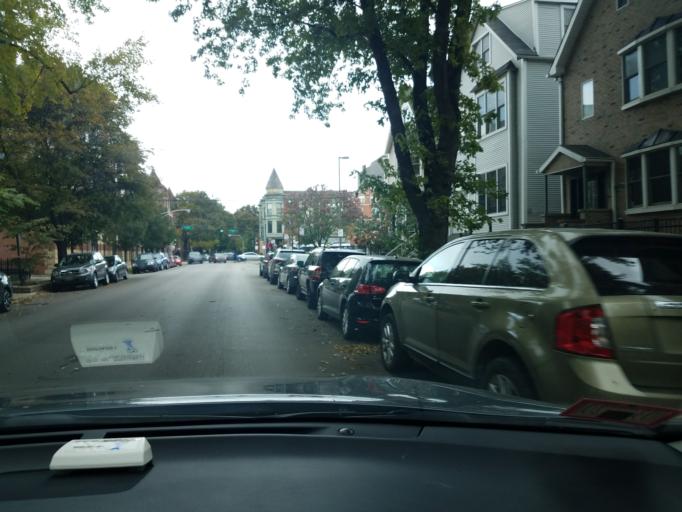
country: US
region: Illinois
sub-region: Cook County
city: Lincolnwood
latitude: 41.9394
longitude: -87.6711
